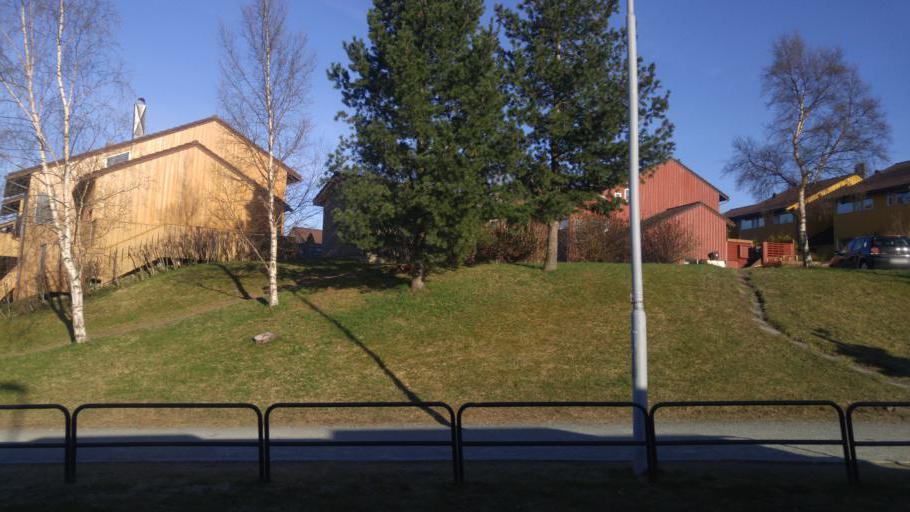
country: NO
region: Sor-Trondelag
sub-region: Trondheim
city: Trondheim
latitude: 63.4175
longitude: 10.4476
